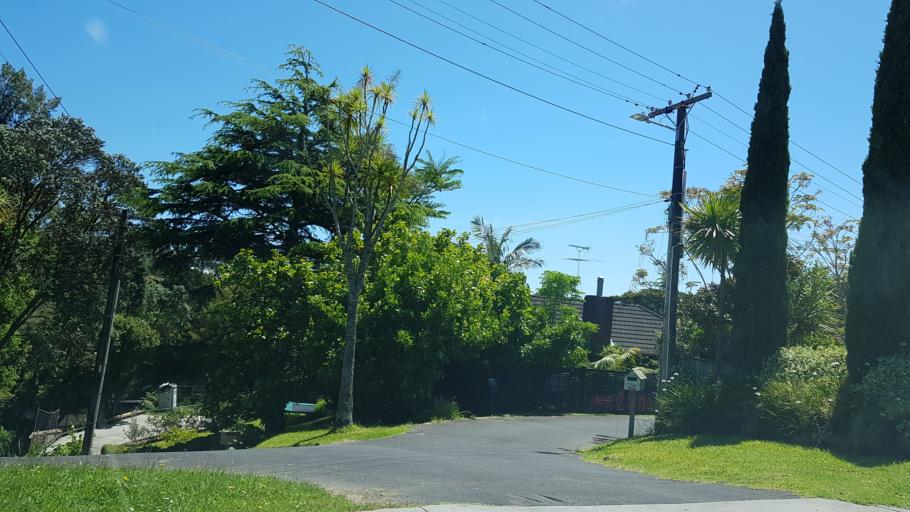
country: NZ
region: Auckland
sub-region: Auckland
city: North Shore
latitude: -36.8076
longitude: 174.7292
